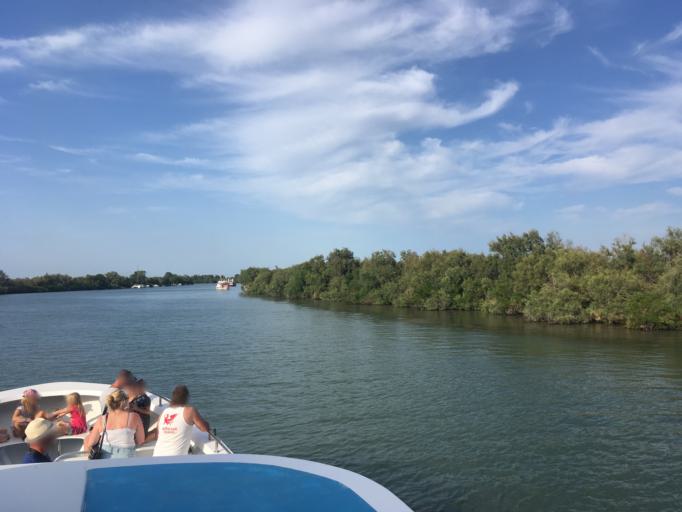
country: FR
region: Provence-Alpes-Cote d'Azur
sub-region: Departement des Bouches-du-Rhone
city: Saintes-Maries-de-la-Mer
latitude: 43.4826
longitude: 4.3787
